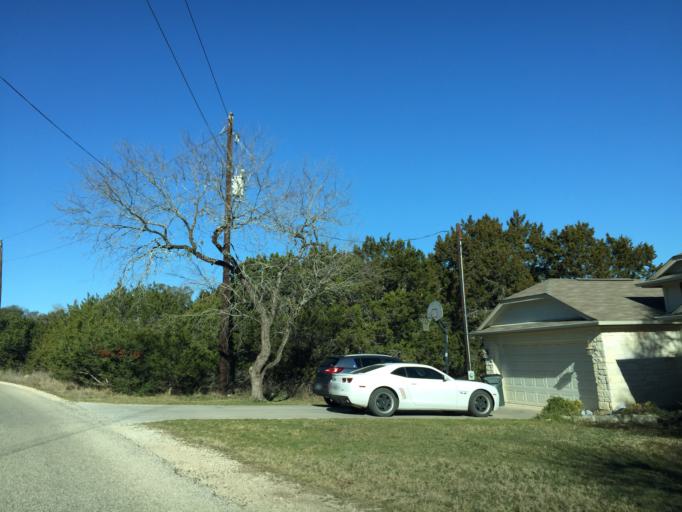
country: US
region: Texas
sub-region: Hays County
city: Woodcreek
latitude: 30.0150
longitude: -98.1190
